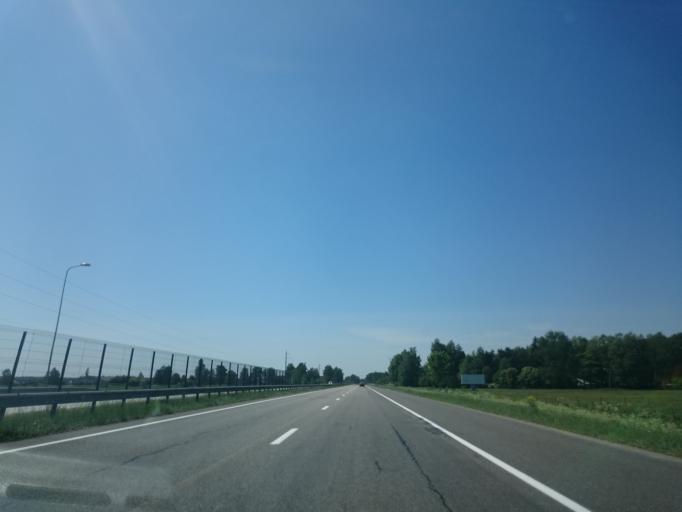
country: LV
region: Marupe
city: Marupe
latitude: 56.8259
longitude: 24.0269
